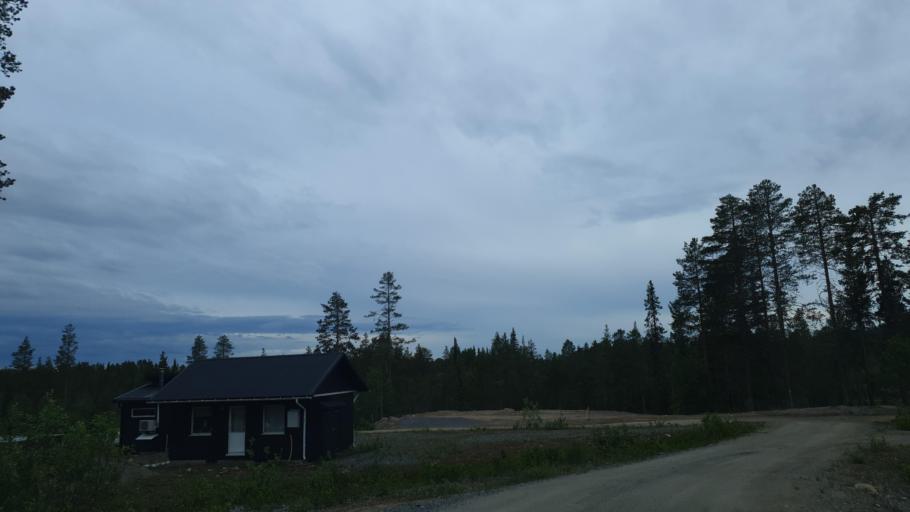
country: SE
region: Norrbotten
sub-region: Jokkmokks Kommun
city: Jokkmokk
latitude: 66.1518
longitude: 19.9939
